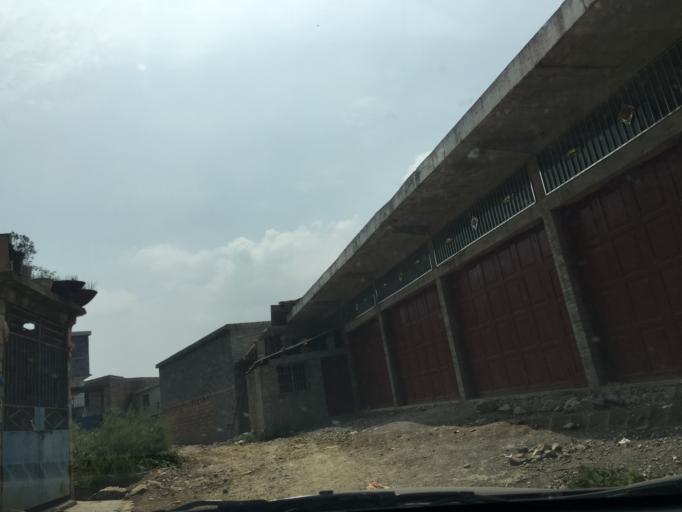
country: CN
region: Guizhou Sheng
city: Anshun
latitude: 25.5971
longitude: 105.6696
